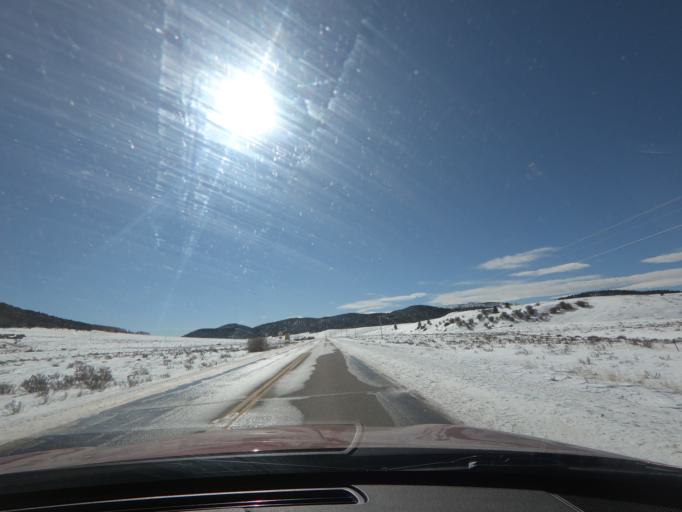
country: US
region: Colorado
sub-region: Teller County
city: Cripple Creek
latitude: 38.7777
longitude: -105.1212
